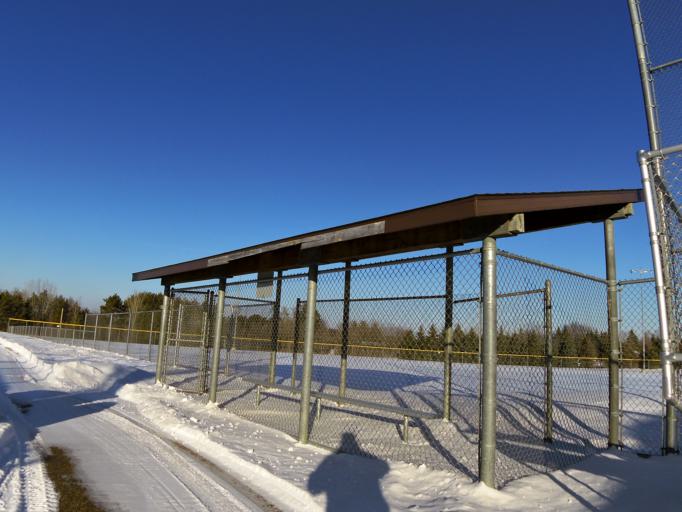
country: US
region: Wisconsin
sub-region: Saint Croix County
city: Hudson
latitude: 44.9793
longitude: -92.7176
